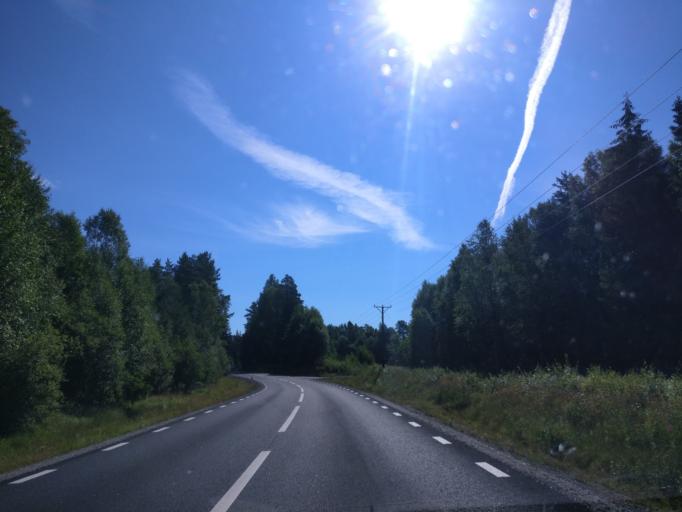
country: SE
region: Vaermland
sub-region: Hagfors Kommun
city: Hagfors
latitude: 60.0341
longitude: 13.8371
